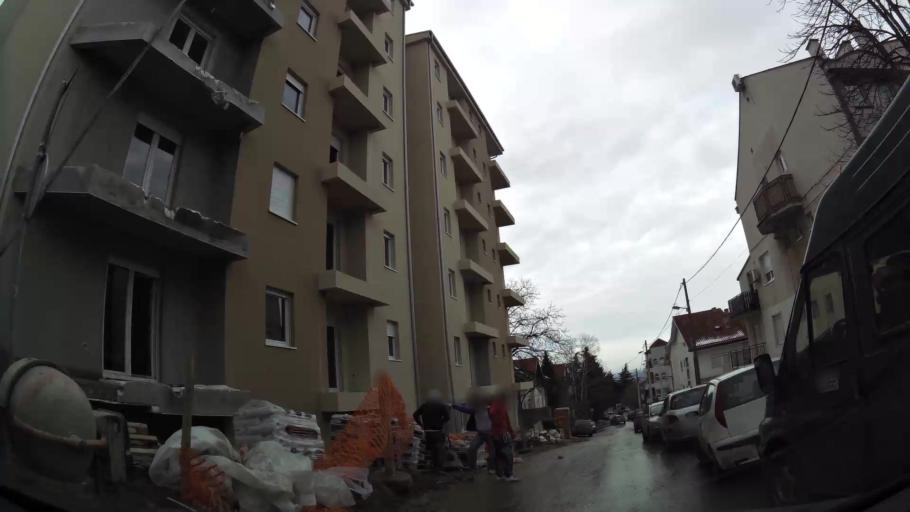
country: RS
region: Central Serbia
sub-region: Belgrade
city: Rakovica
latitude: 44.7527
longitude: 20.4164
